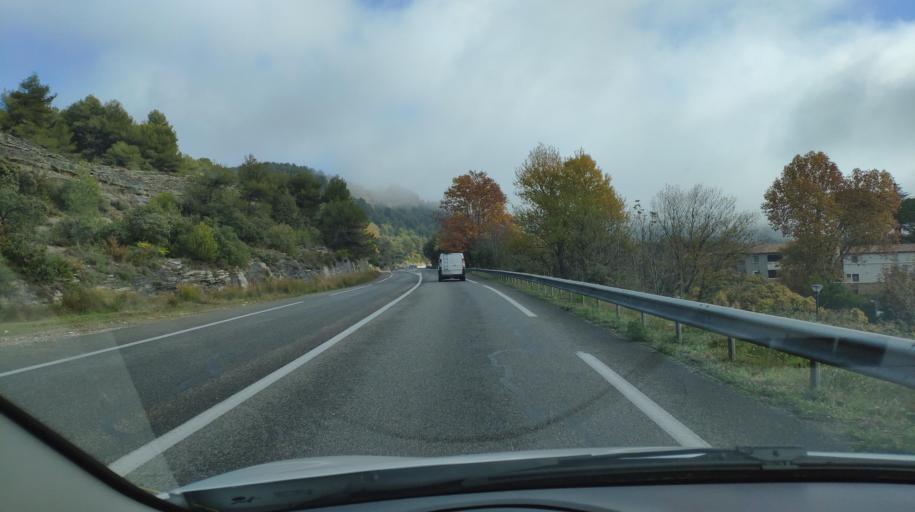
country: FR
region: Provence-Alpes-Cote d'Azur
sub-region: Departement du Vaucluse
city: Menerbes
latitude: 43.8588
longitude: 5.2112
